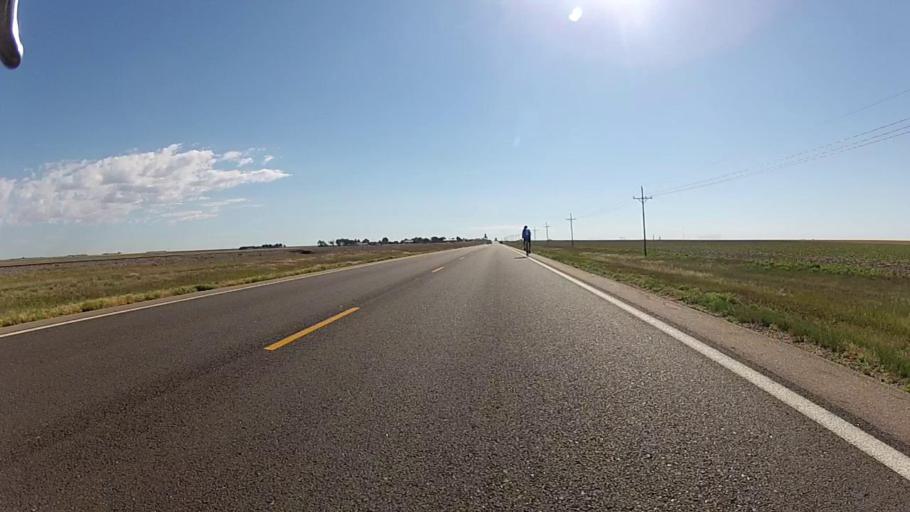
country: US
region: Kansas
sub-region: Gray County
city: Cimarron
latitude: 37.5871
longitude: -100.4862
